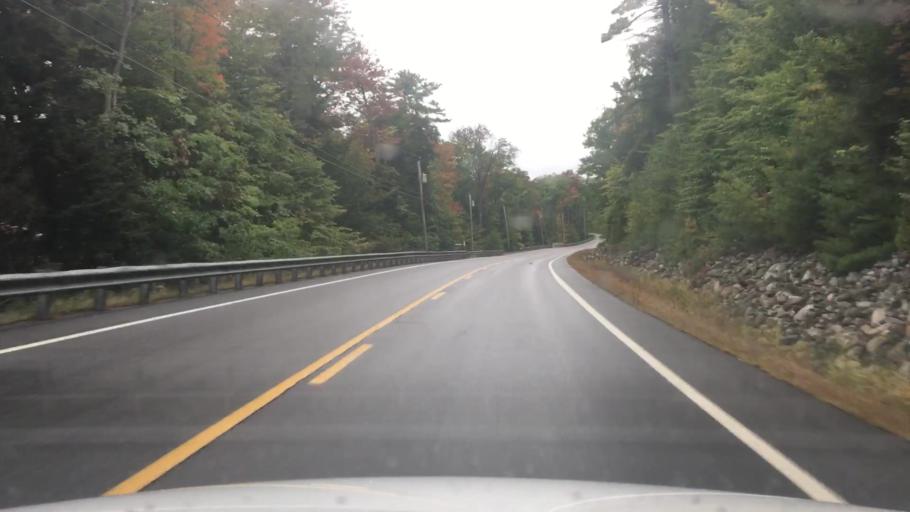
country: US
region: Maine
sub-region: Kennebec County
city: Rome
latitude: 44.5467
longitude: -69.8944
